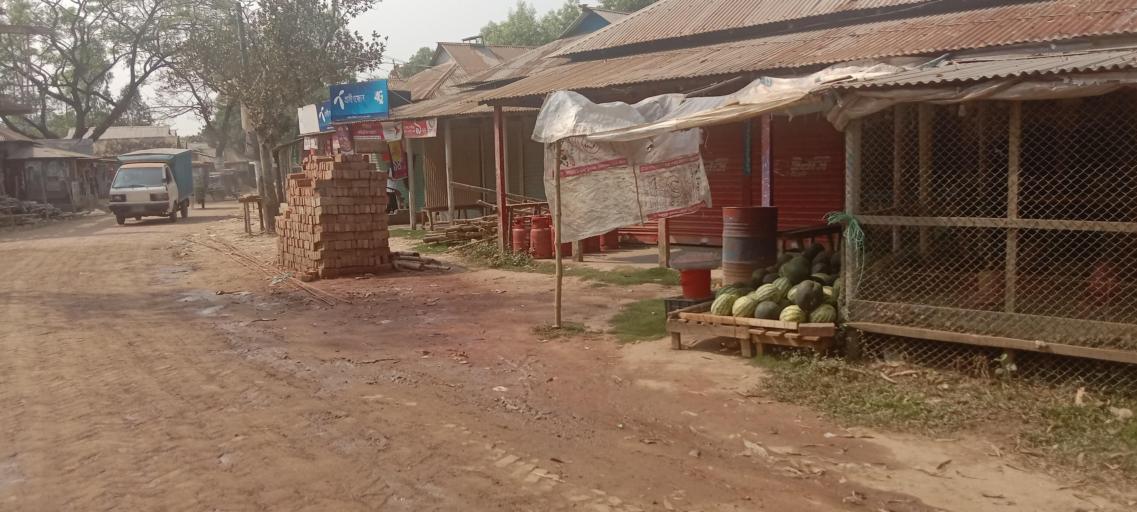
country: BD
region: Dhaka
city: Sakhipur
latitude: 24.3339
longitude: 90.2875
